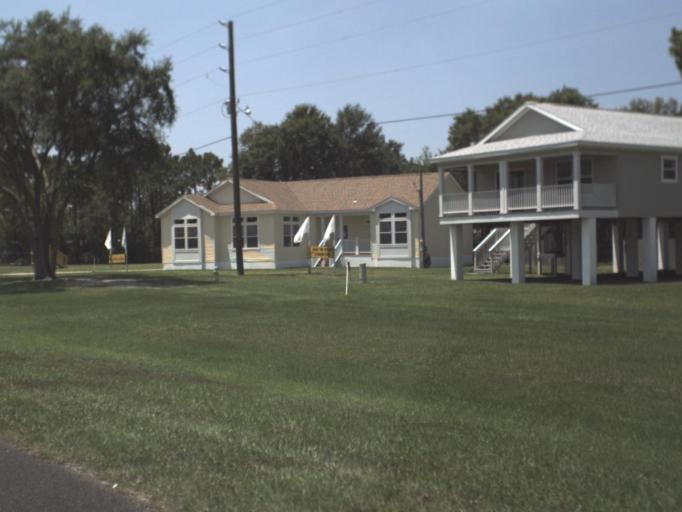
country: US
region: Florida
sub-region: Citrus County
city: Sugarmill Woods
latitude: 28.7391
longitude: -82.5530
